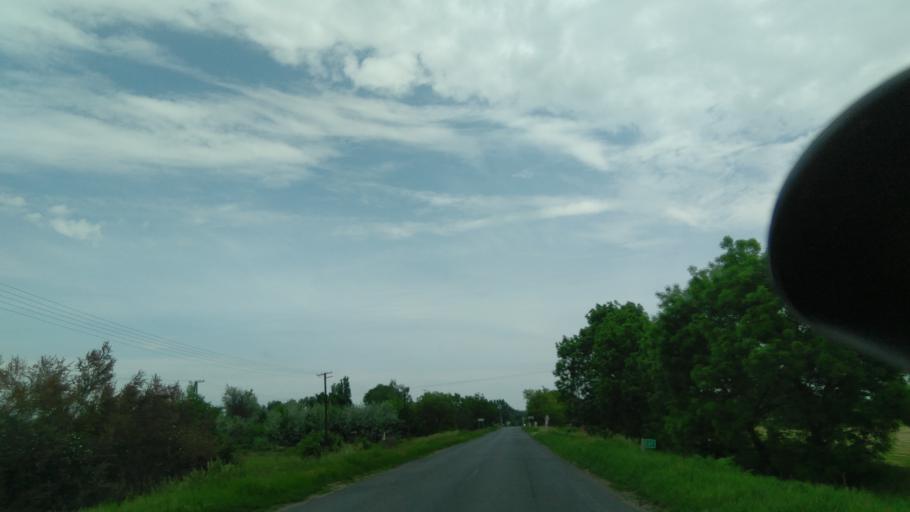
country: HU
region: Bekes
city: Fuzesgyarmat
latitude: 47.0883
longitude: 21.2010
